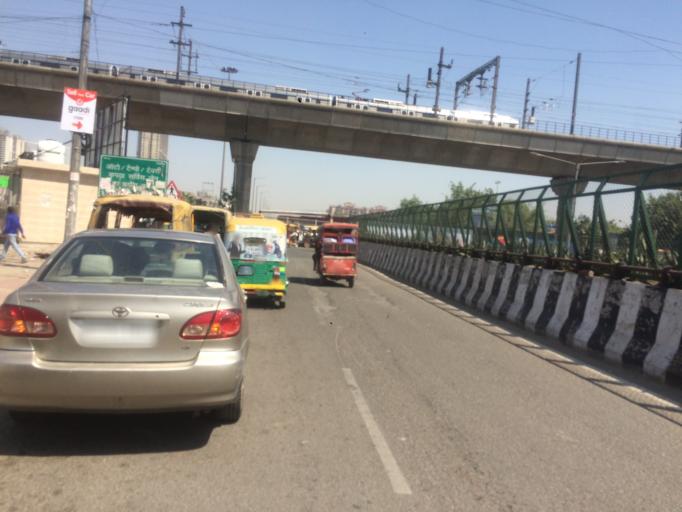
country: IN
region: Uttar Pradesh
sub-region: Gautam Buddha Nagar
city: Noida
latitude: 28.5750
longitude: 77.3575
